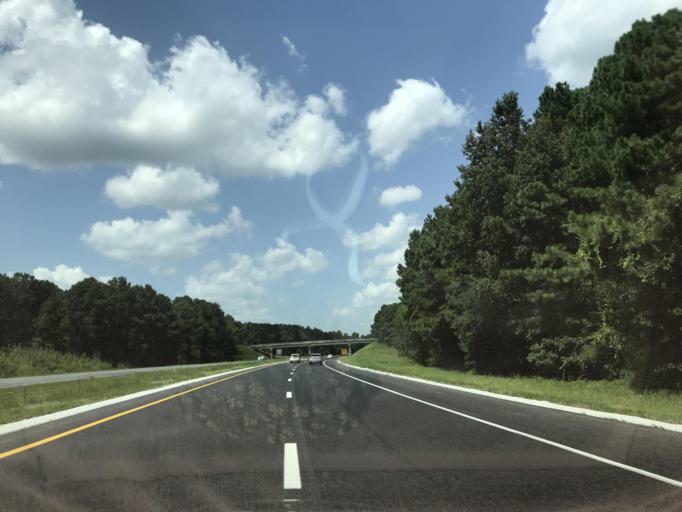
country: US
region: North Carolina
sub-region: Duplin County
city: Warsaw
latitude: 34.9573
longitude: -78.1008
